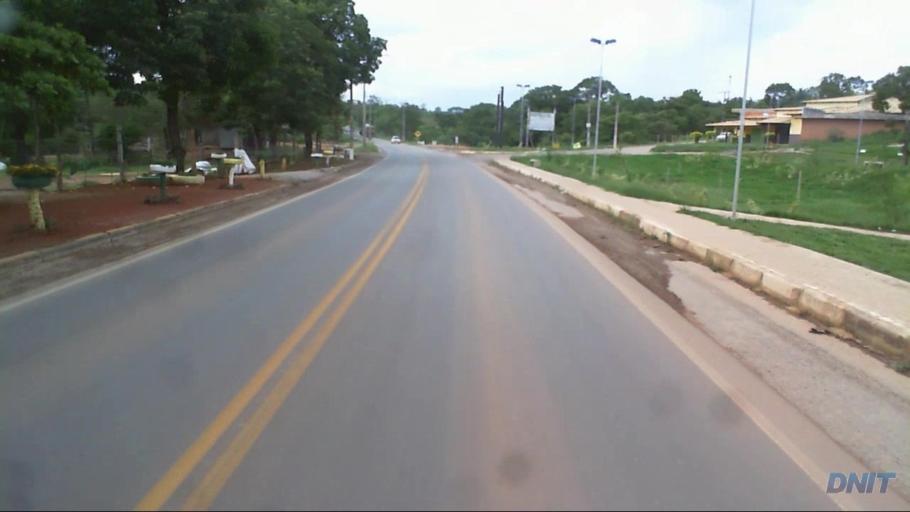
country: BR
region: Goias
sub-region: Padre Bernardo
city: Padre Bernardo
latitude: -15.1763
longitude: -48.2860
